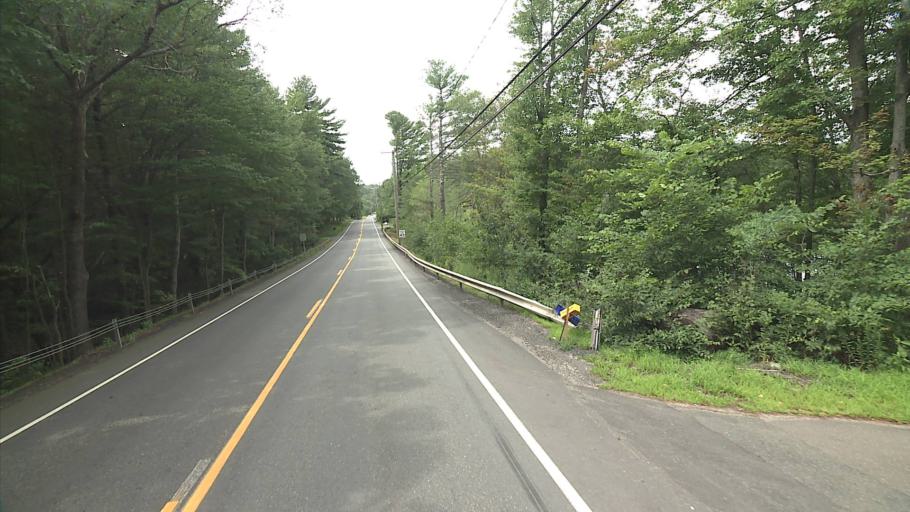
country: US
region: Connecticut
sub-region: Tolland County
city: Storrs
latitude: 41.8787
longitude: -72.2793
